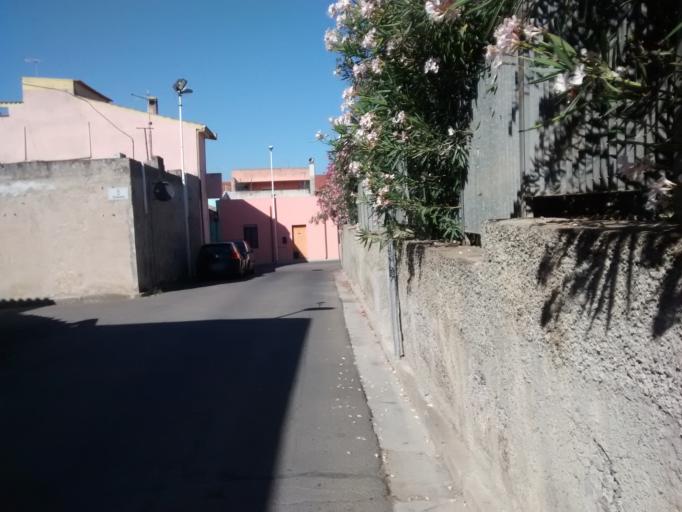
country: IT
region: Sardinia
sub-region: Provincia di Cagliari
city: Soleminis
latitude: 39.3464
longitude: 9.1795
